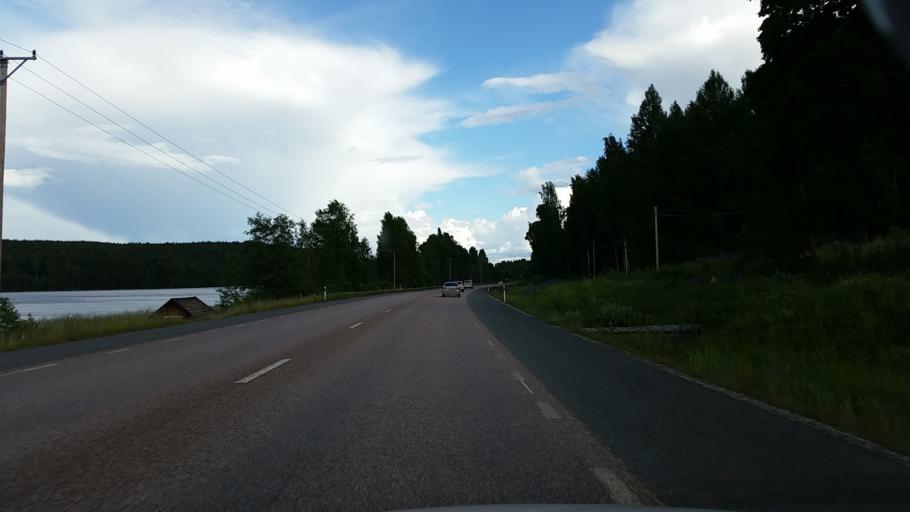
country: SE
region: Vaestmanland
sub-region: Fagersta Kommun
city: Fagersta
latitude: 60.0056
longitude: 15.6547
